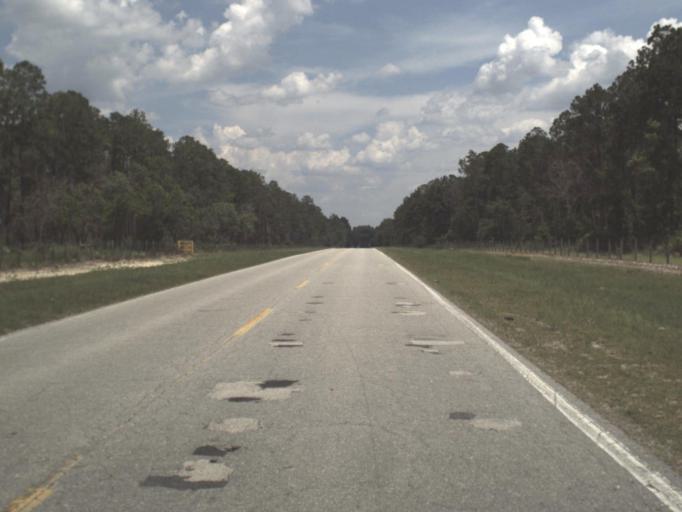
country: US
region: Florida
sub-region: Bradford County
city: Starke
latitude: 29.9871
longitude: -82.0194
